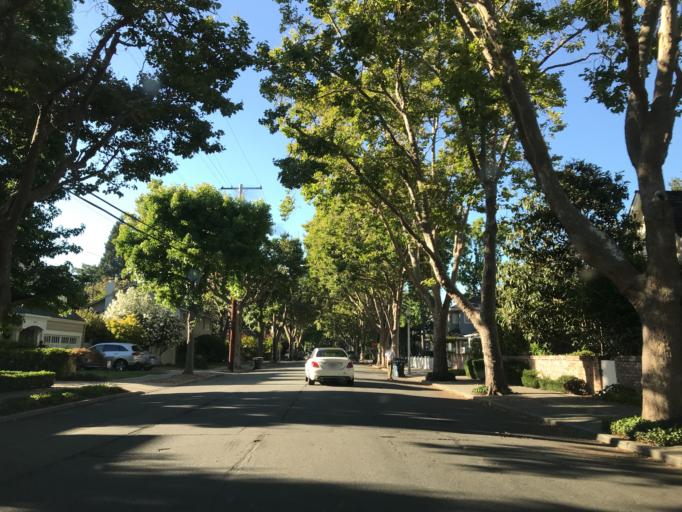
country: US
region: California
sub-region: Santa Clara County
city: Palo Alto
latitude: 37.4518
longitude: -122.1469
